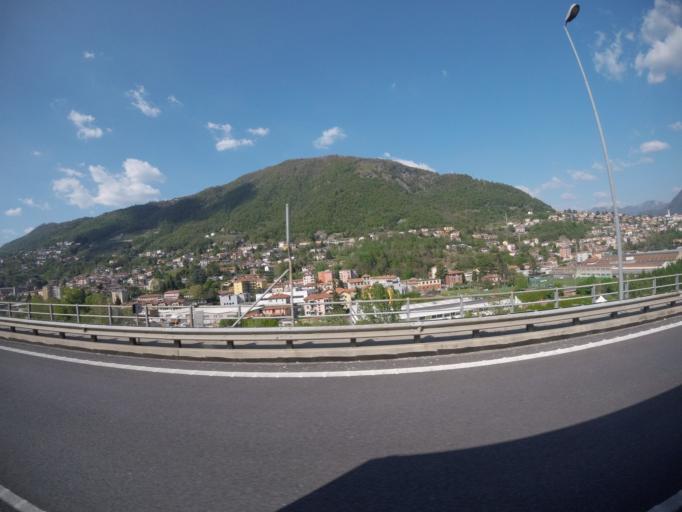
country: IT
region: Lombardy
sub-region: Provincia di Como
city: Maslianico
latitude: 45.8386
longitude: 9.0493
